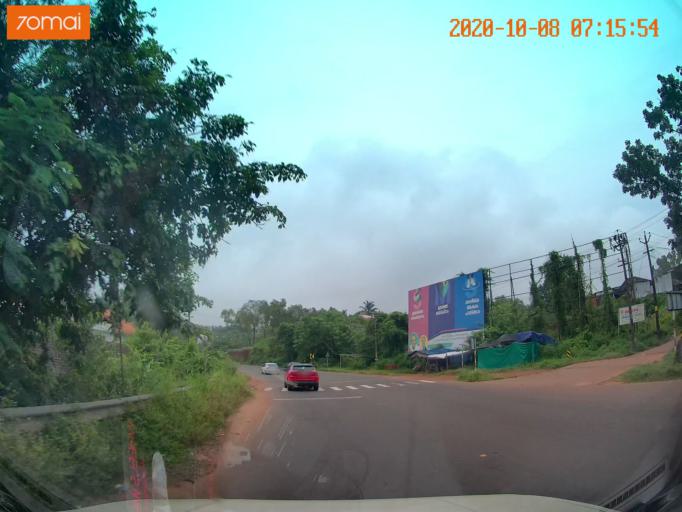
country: IN
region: Kerala
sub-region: Malappuram
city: Ponnani
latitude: 10.8283
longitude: 76.0195
